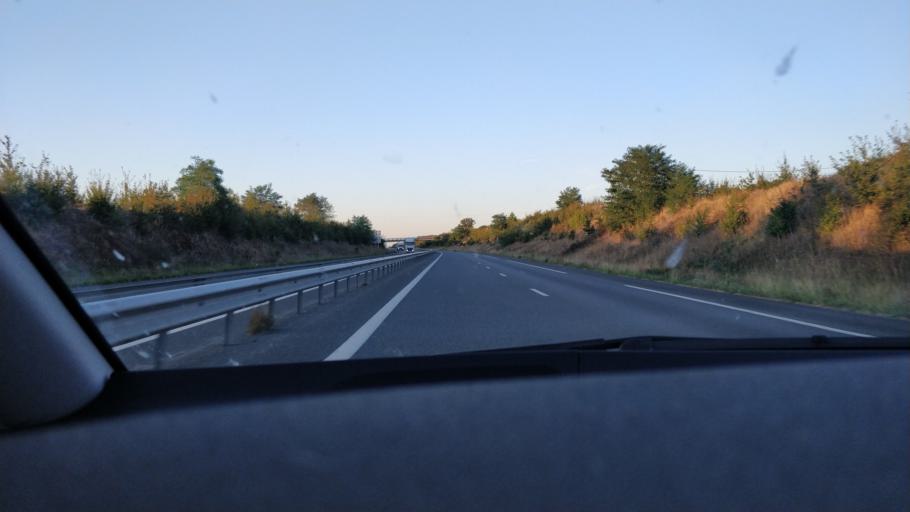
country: FR
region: Poitou-Charentes
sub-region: Departement de la Charente
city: La Rochefoucauld
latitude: 45.7595
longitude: 0.3929
